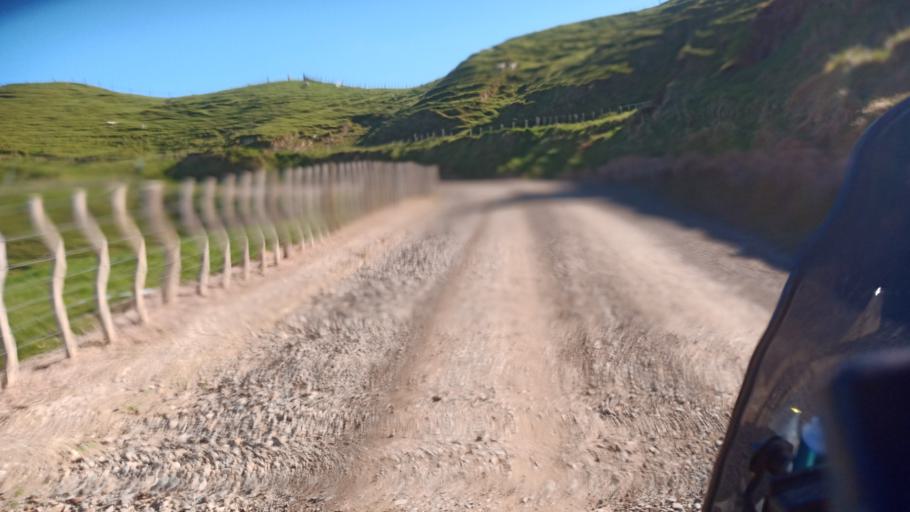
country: NZ
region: Gisborne
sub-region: Gisborne District
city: Gisborne
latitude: -39.1664
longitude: 177.8979
